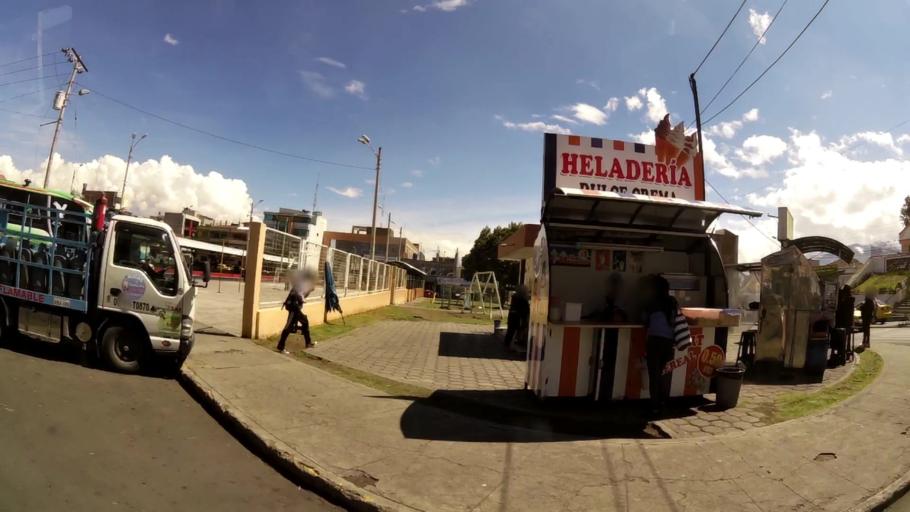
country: EC
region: Chimborazo
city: Riobamba
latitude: -1.6798
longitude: -78.6419
